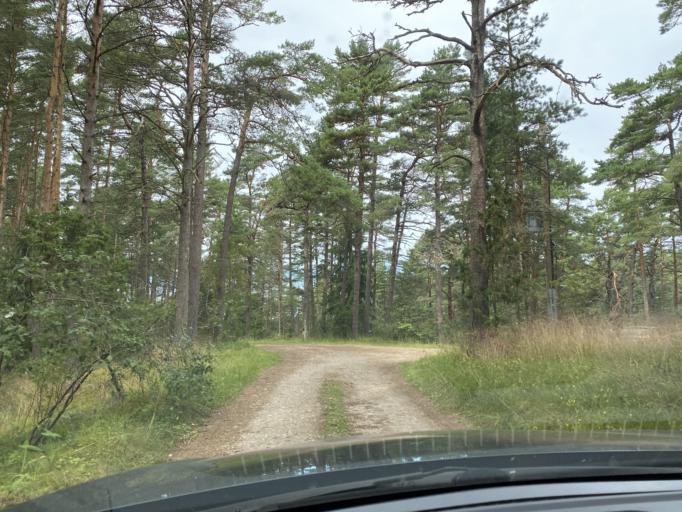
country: LV
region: Ventspils
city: Ventspils
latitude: 57.2090
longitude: 21.4184
